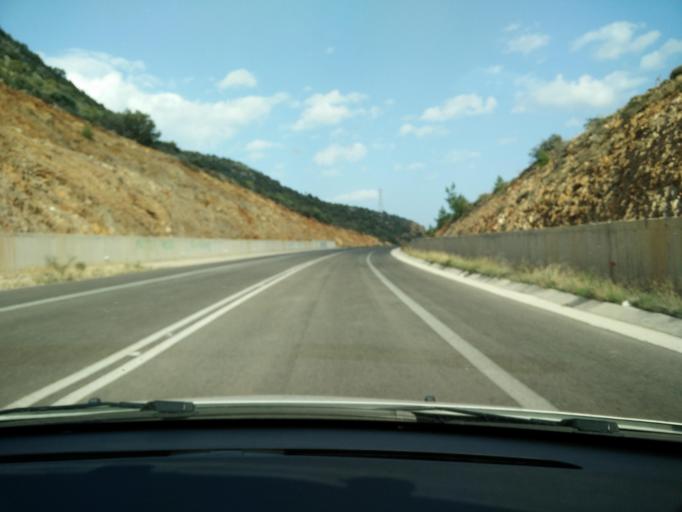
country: GR
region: Crete
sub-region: Nomos Lasithiou
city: Agios Nikolaos
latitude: 35.1485
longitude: 25.7082
